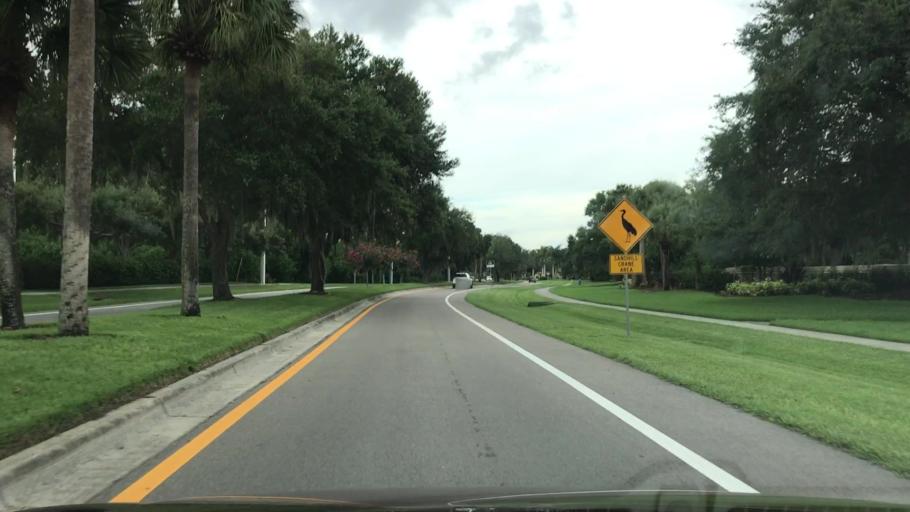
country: US
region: Florida
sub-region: Sarasota County
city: Vamo
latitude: 27.2446
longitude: -82.4738
